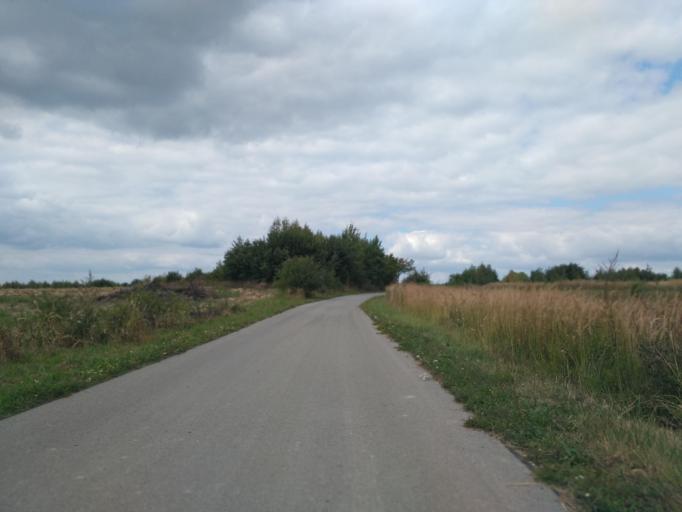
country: PL
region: Subcarpathian Voivodeship
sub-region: Powiat rzeszowski
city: Dynow
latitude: 49.7701
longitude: 22.2845
